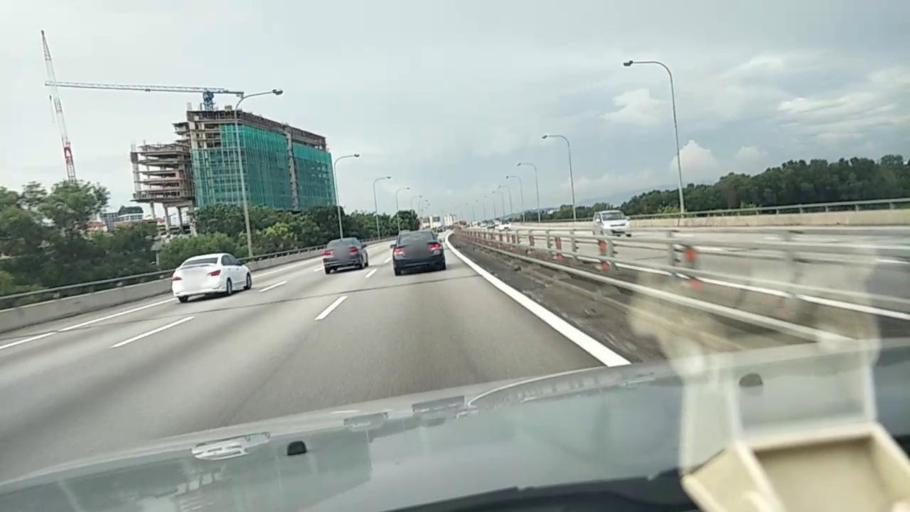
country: MY
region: Selangor
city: Shah Alam
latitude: 3.0807
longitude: 101.5515
